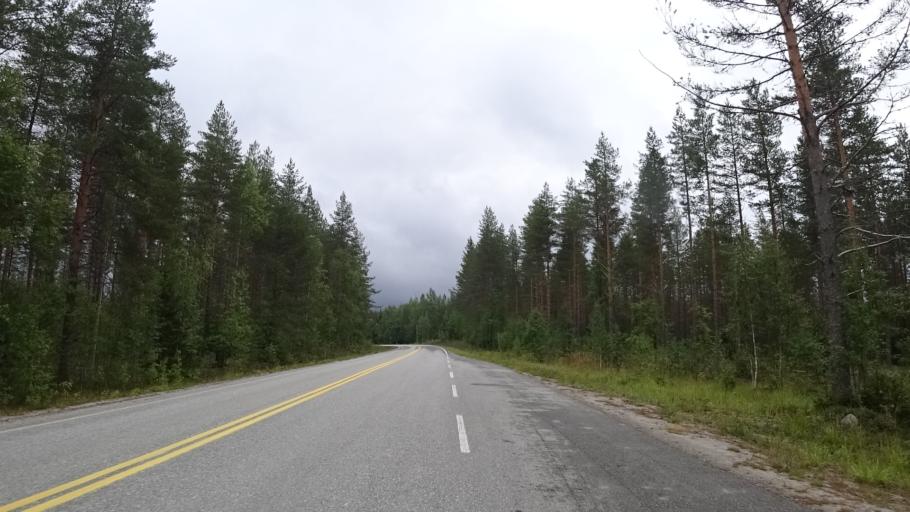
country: FI
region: North Karelia
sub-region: Joensuu
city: Ilomantsi
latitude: 63.2509
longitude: 30.7101
